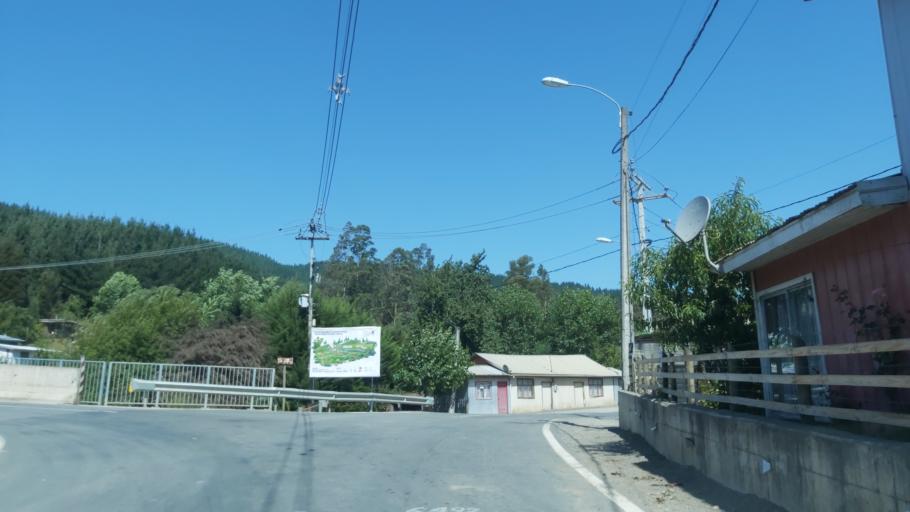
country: CL
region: Biobio
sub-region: Provincia de Concepcion
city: Tome
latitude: -36.5553
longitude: -72.8657
